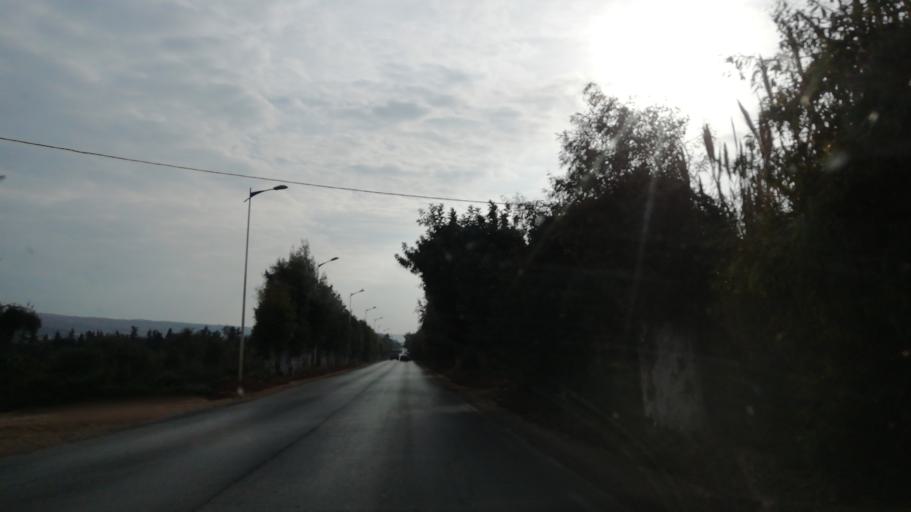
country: DZ
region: Mostaganem
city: Mostaganem
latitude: 35.8736
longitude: 0.0777
